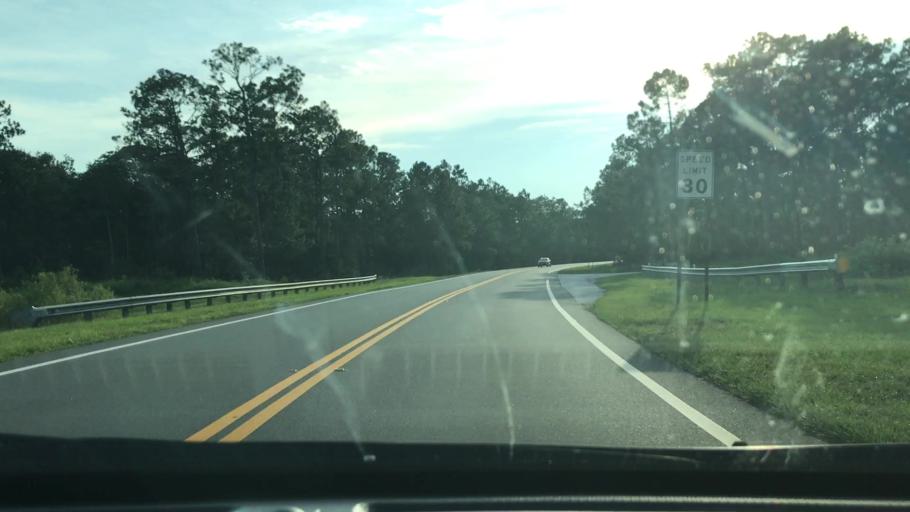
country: US
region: Florida
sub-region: Osceola County
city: Celebration
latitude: 28.3910
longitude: -81.5615
